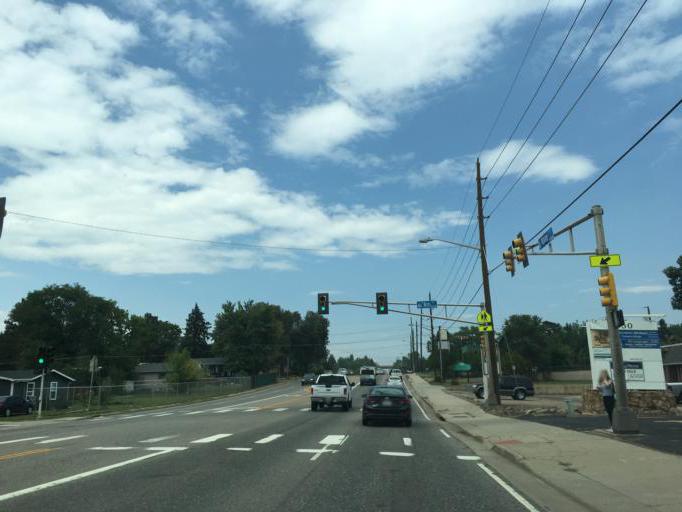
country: US
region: Colorado
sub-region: Jefferson County
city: Lakewood
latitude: 39.7297
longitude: -105.1096
